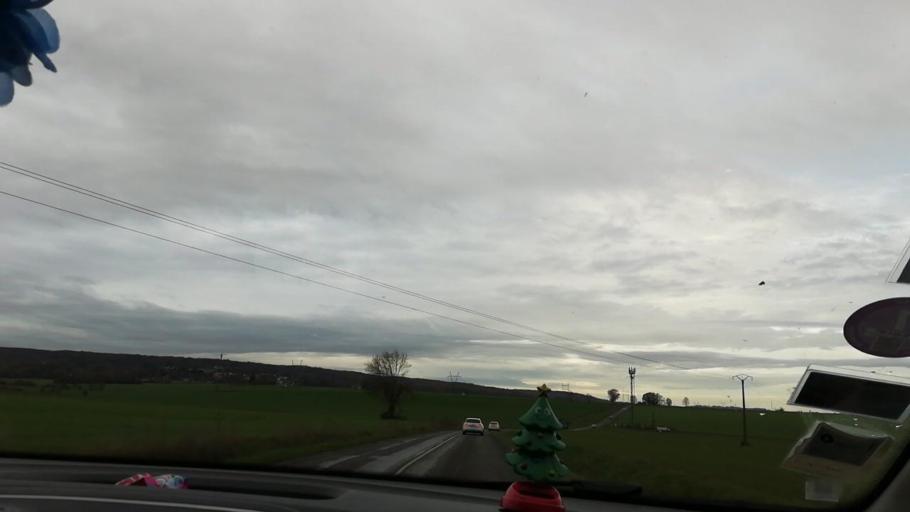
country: FR
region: Ile-de-France
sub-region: Departement de Seine-et-Marne
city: Juilly
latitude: 49.0158
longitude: 2.7230
